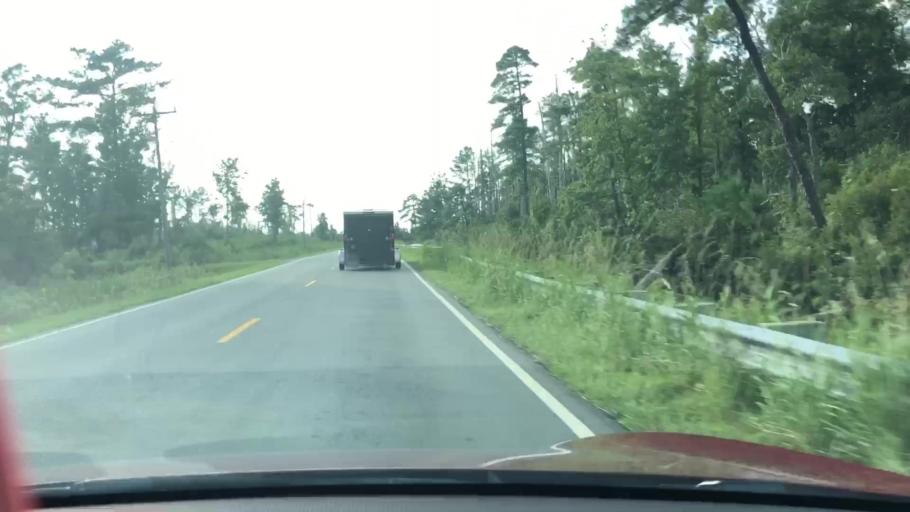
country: US
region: North Carolina
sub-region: Dare County
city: Wanchese
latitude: 35.6156
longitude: -75.8308
